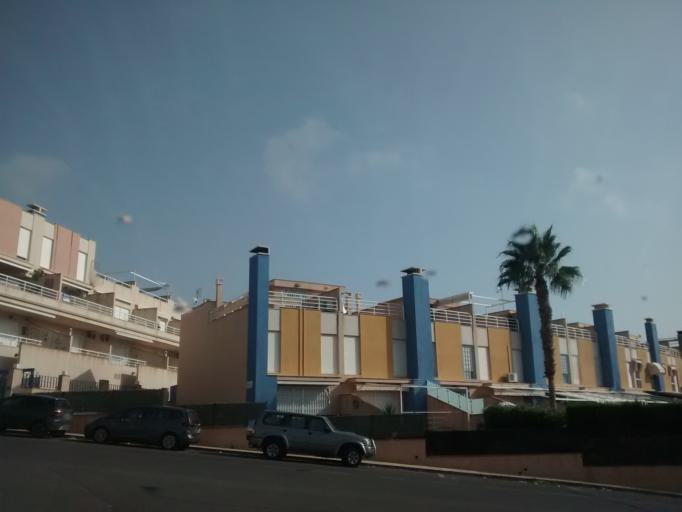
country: ES
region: Valencia
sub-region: Provincia de Alicante
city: Pilar de la Horadada
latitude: 37.9073
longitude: -0.7447
